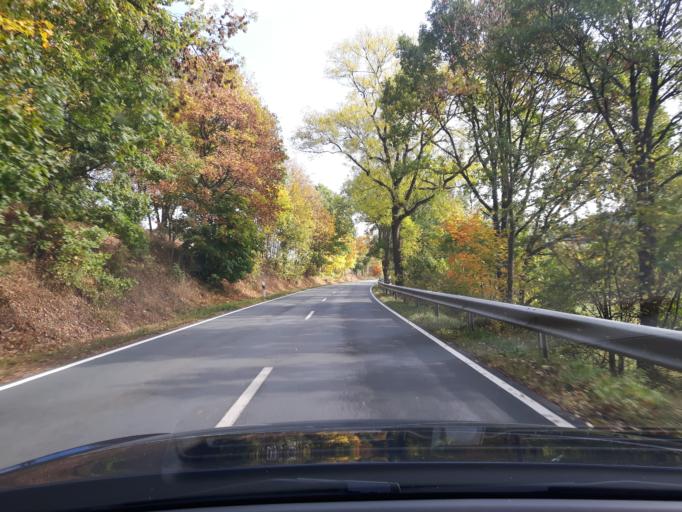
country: DE
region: North Rhine-Westphalia
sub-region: Regierungsbezirk Arnsberg
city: Bad Berleburg
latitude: 51.0208
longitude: 8.4498
